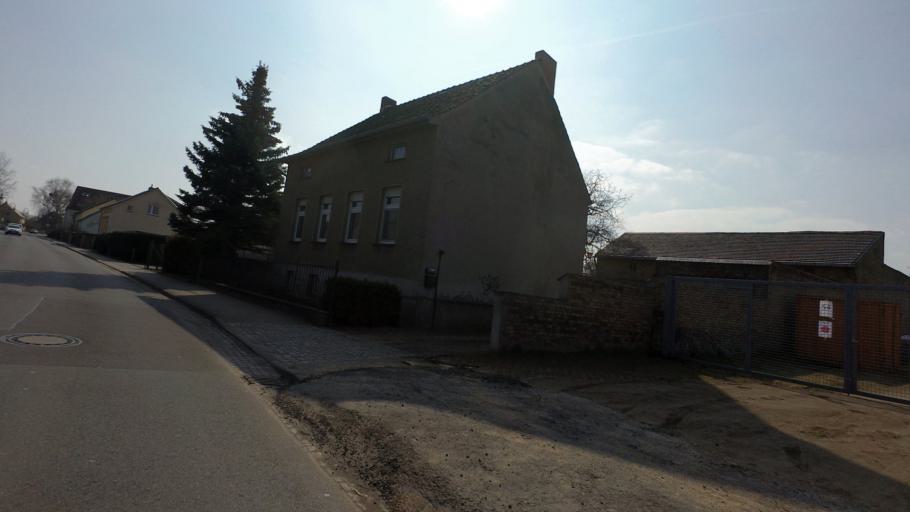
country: DE
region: Brandenburg
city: Werder
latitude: 52.3682
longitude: 12.9380
